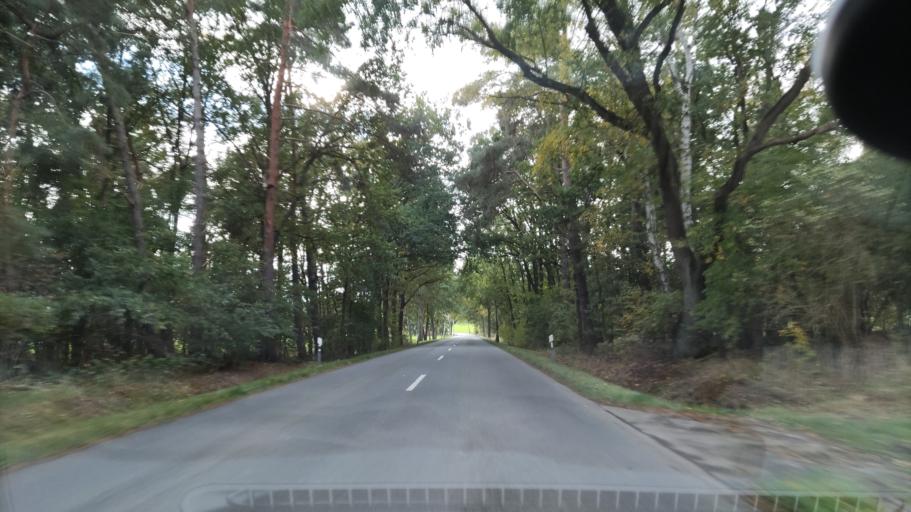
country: DE
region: Lower Saxony
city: Romstedt
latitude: 53.0865
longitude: 10.6428
